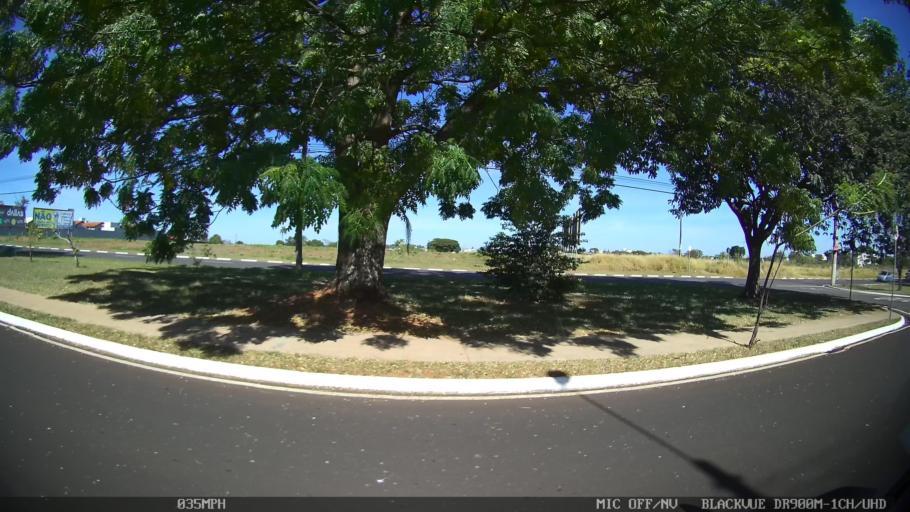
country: BR
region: Sao Paulo
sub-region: Franca
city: Franca
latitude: -20.5594
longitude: -47.3760
